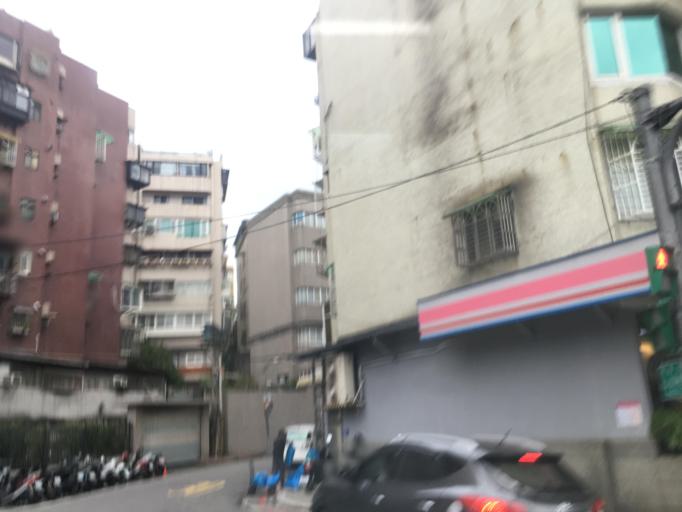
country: TW
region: Taipei
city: Taipei
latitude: 25.1290
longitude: 121.5284
